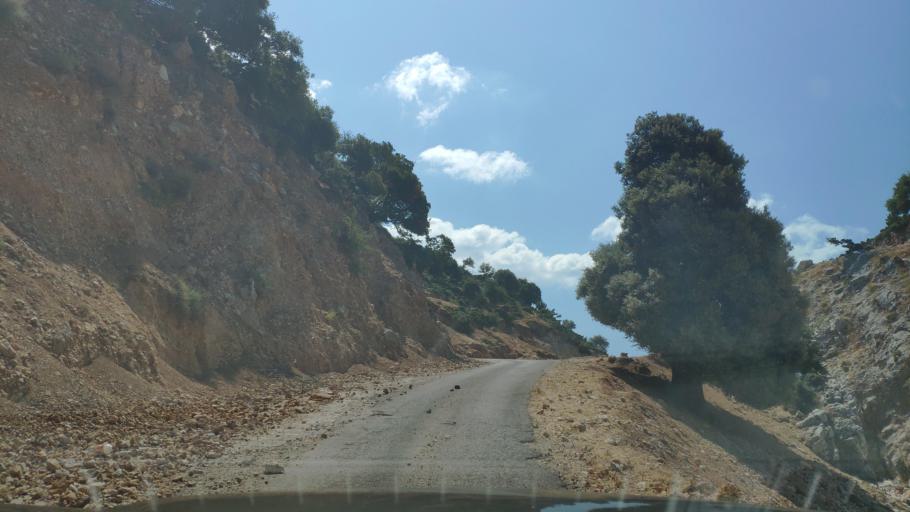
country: GR
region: West Greece
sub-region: Nomos Aitolias kai Akarnanias
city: Monastirakion
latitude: 38.8112
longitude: 20.9400
